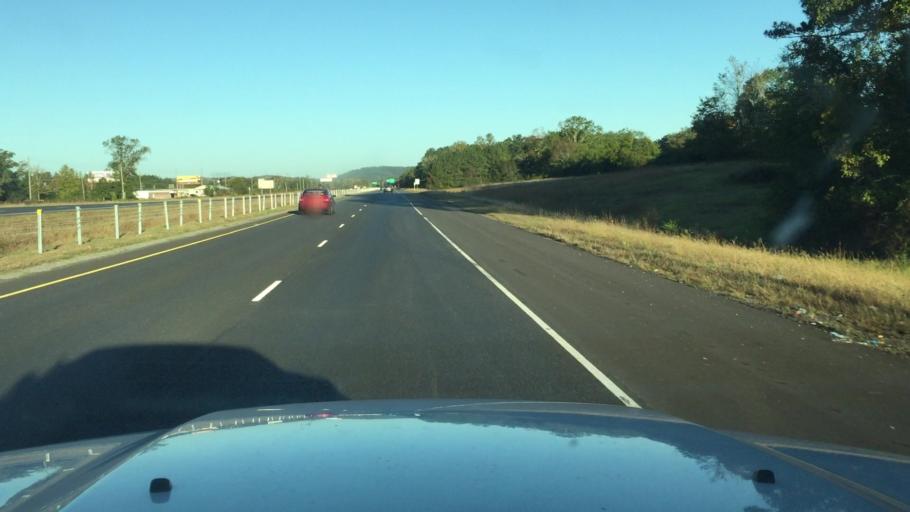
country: US
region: Alabama
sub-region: Etowah County
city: Rainbow City
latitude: 33.9935
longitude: -86.0463
